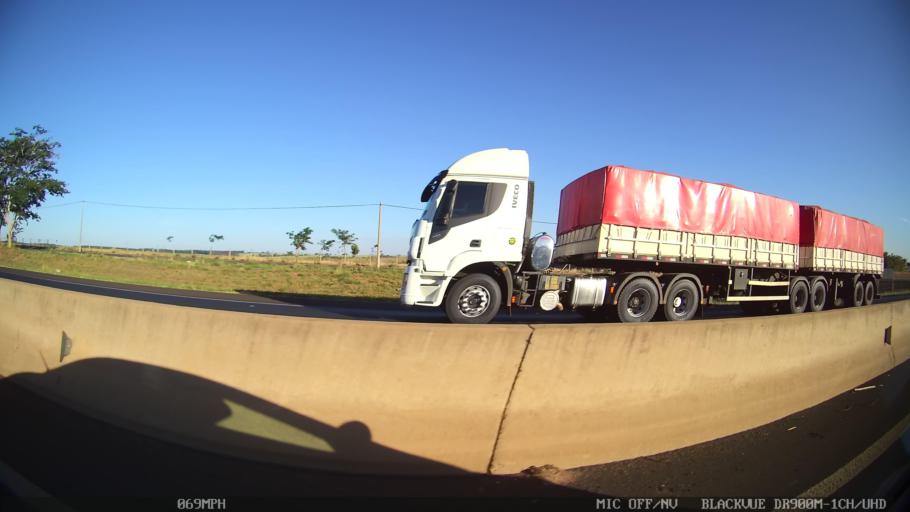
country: BR
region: Sao Paulo
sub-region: Sao Jose Do Rio Preto
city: Sao Jose do Rio Preto
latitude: -20.7937
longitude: -49.3089
